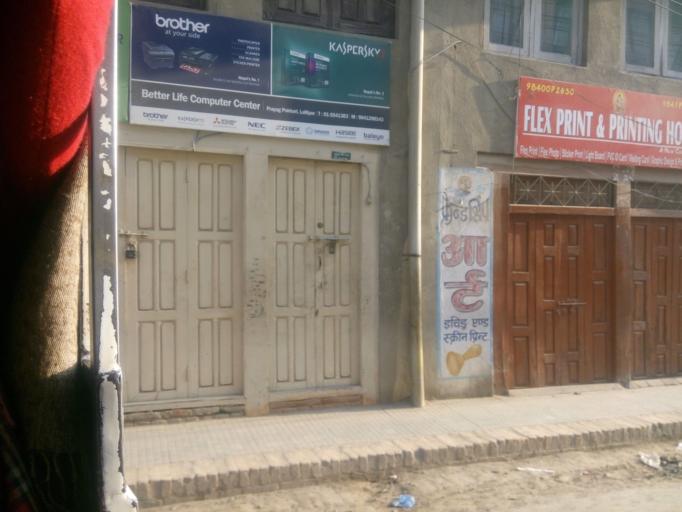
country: NP
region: Central Region
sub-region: Bagmati Zone
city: Patan
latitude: 27.6684
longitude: 85.3258
